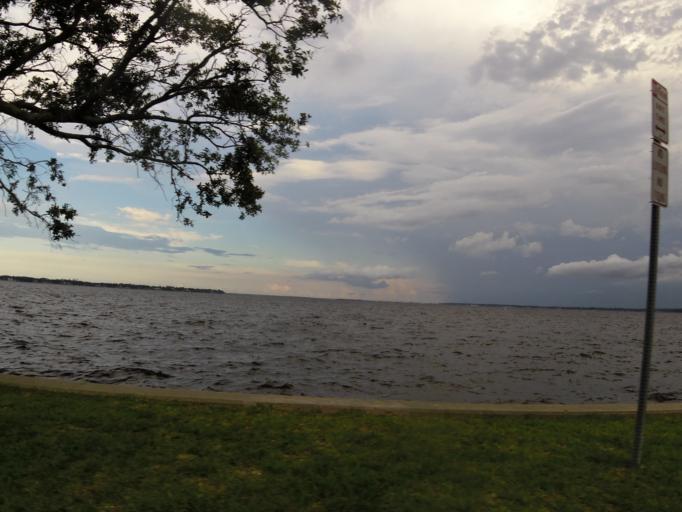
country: US
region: Florida
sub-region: Duval County
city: Jacksonville
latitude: 30.3093
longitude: -81.6822
